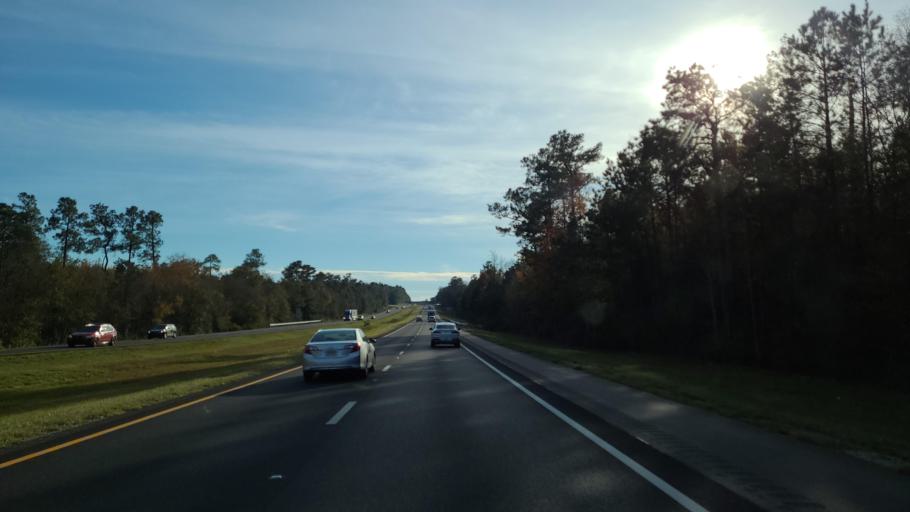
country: US
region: Mississippi
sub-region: Lamar County
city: Purvis
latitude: 31.1505
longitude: -89.3629
